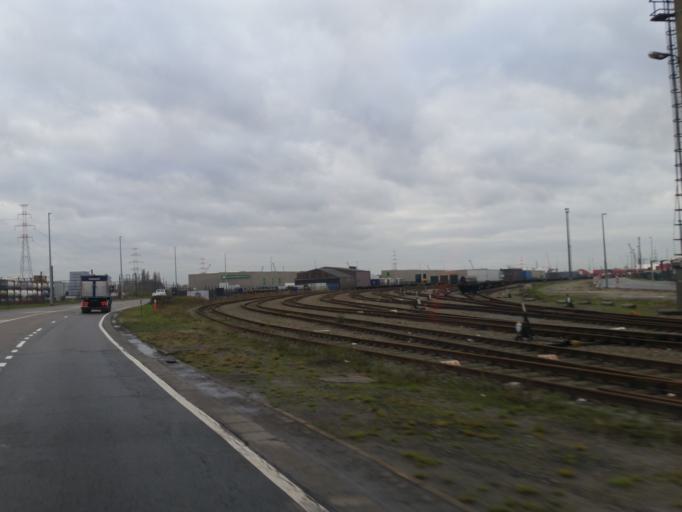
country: BE
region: Flanders
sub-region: Provincie Antwerpen
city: Stabroek
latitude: 51.2768
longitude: 4.3850
